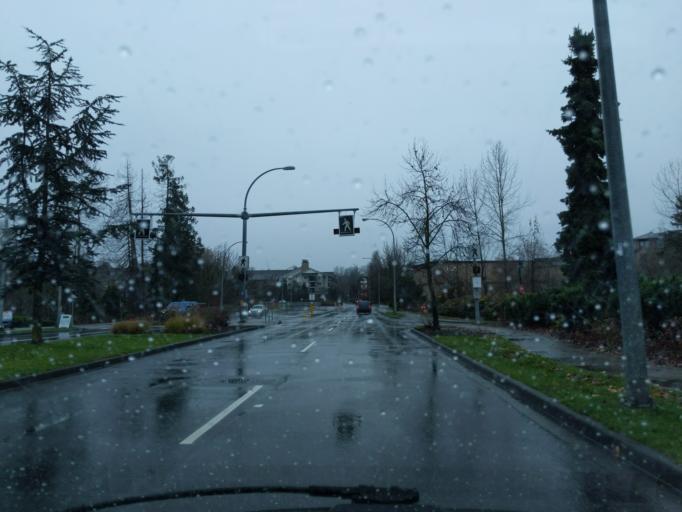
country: CA
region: British Columbia
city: Walnut Grove
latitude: 49.1672
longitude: -122.6627
